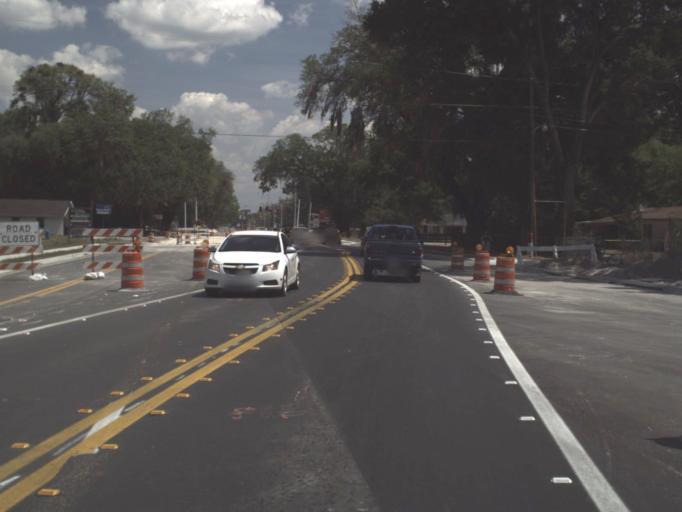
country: US
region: Florida
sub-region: Sumter County
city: Bushnell
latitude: 28.6686
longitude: -82.1235
